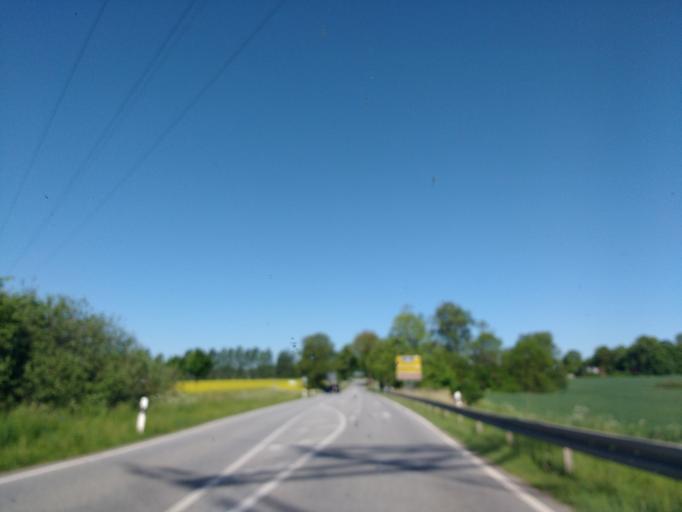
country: DE
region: Mecklenburg-Vorpommern
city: Hornstorf
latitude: 53.8843
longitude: 11.5488
